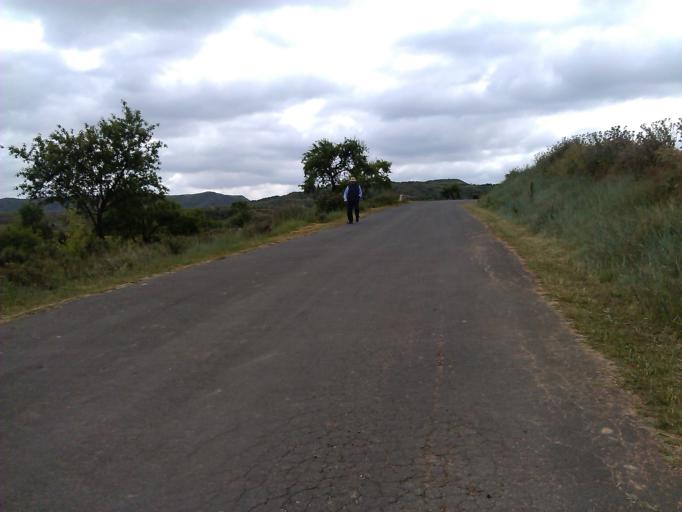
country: ES
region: La Rioja
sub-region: Provincia de La Rioja
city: Navarrete
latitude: 42.4384
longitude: -2.5147
